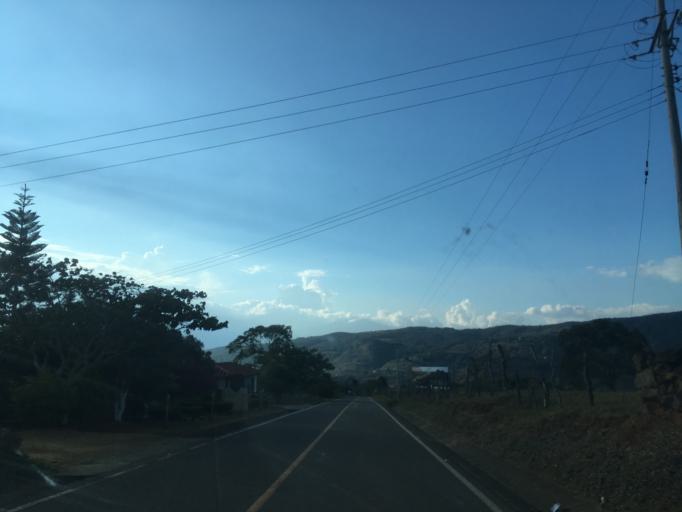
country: CO
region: Santander
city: Villanueva
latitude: 6.6397
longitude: -73.1870
